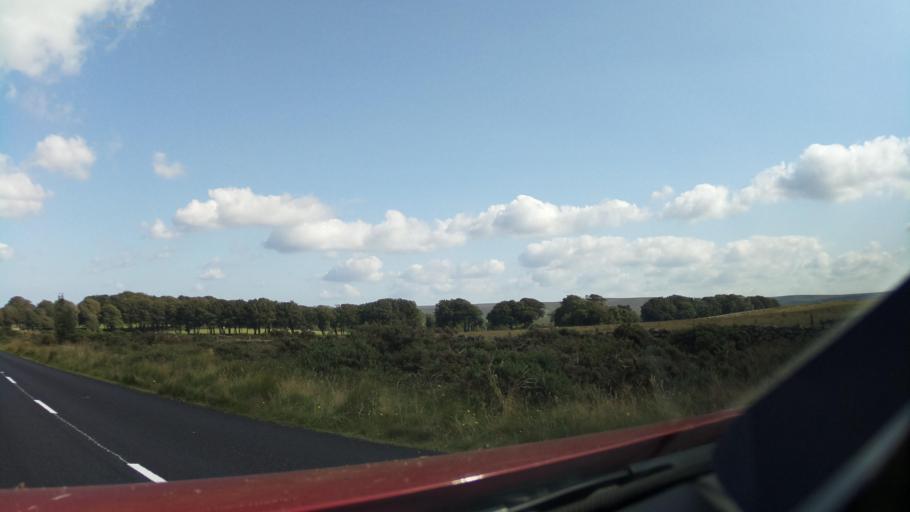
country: GB
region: England
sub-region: Devon
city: Yelverton
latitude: 50.5561
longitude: -3.9485
